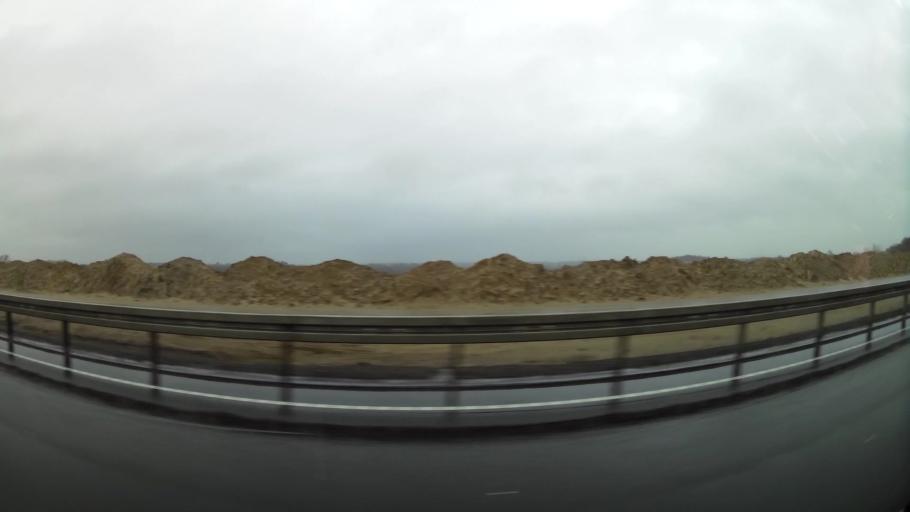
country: DK
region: Central Jutland
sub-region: Herning Kommune
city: Avlum
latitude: 56.2273
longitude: 8.8235
